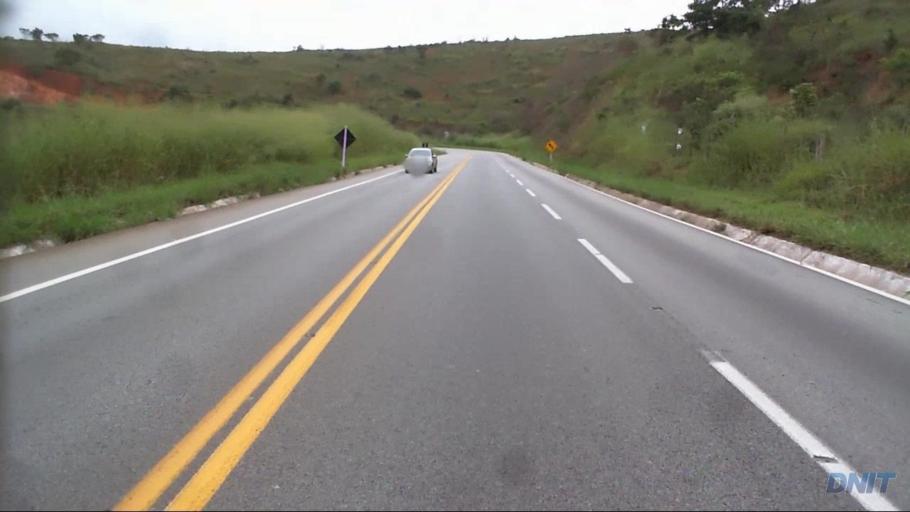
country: BR
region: Minas Gerais
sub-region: Nova Era
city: Nova Era
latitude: -19.7922
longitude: -43.0556
